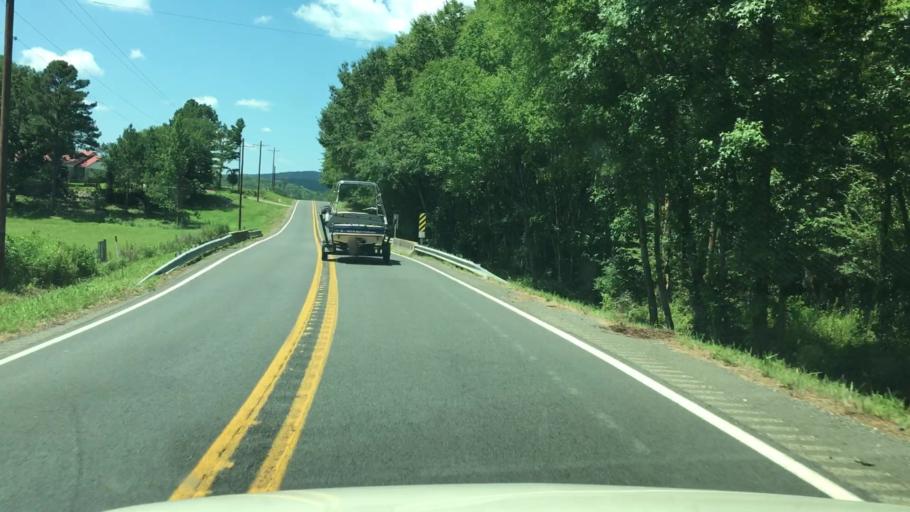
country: US
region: Arkansas
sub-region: Garland County
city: Lake Hamilton
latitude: 34.3302
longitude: -93.1746
